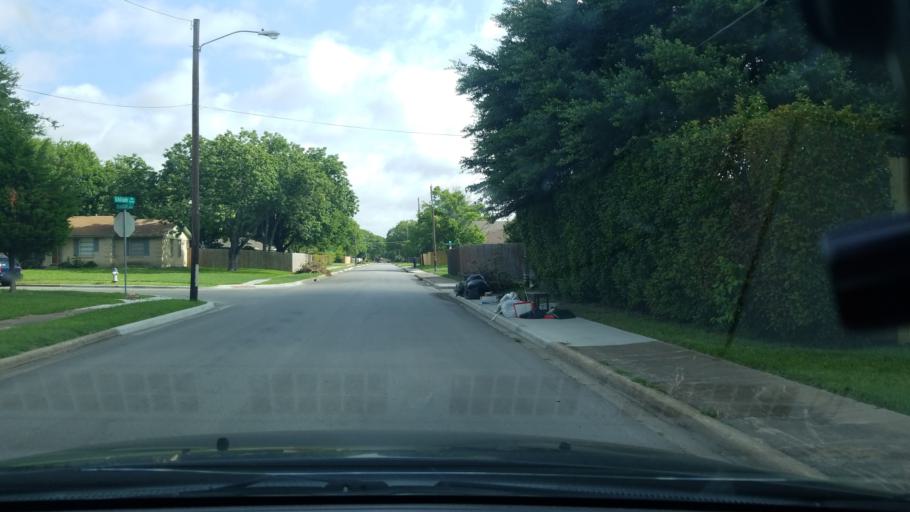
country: US
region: Texas
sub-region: Dallas County
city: Mesquite
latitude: 32.8165
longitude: -96.6684
